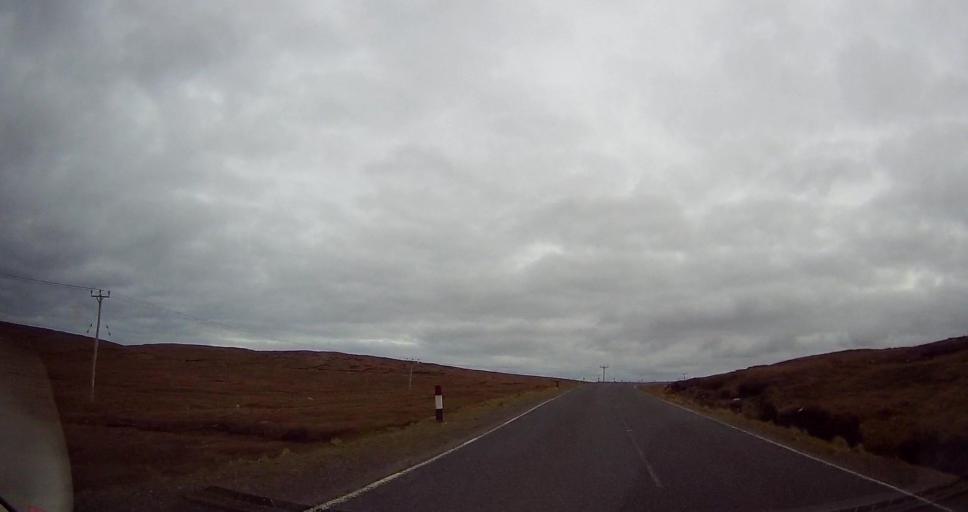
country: GB
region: Scotland
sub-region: Shetland Islands
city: Shetland
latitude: 60.6334
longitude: -1.0662
